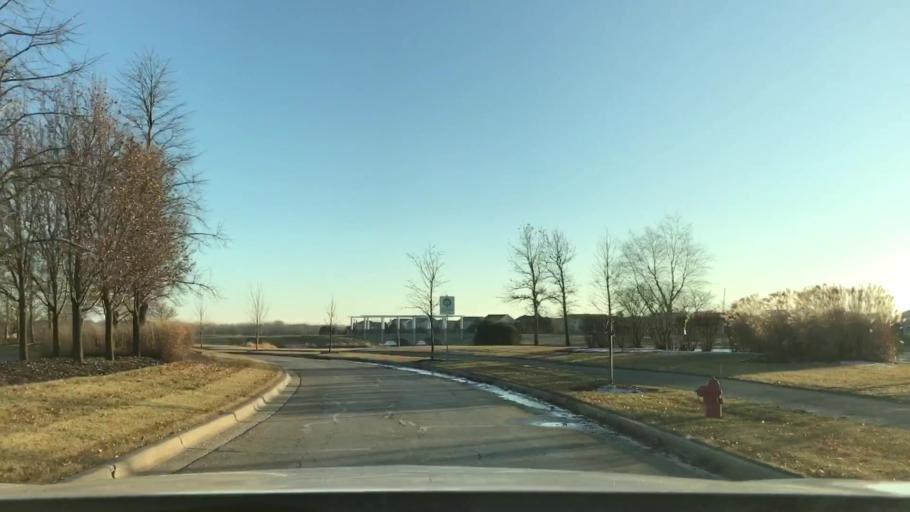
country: US
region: Illinois
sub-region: Kane County
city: Pingree Grove
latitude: 42.0880
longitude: -88.4374
